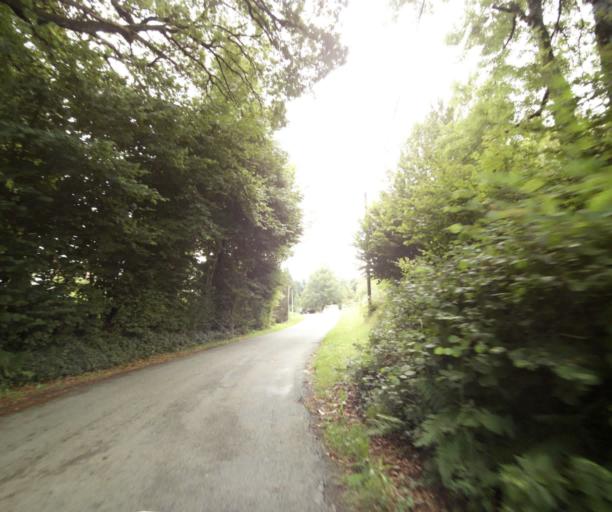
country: FR
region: Limousin
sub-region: Departement de la Correze
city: Sainte-Fortunade
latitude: 45.1931
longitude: 1.8108
